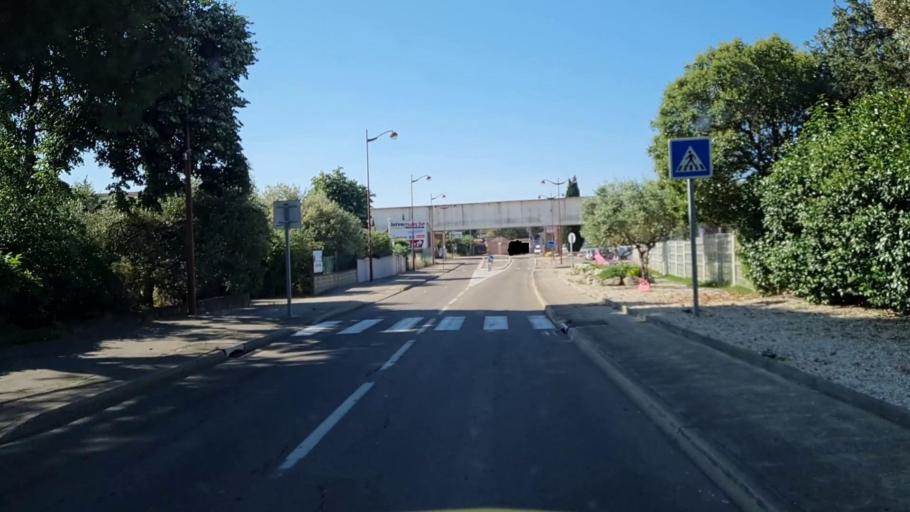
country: FR
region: Languedoc-Roussillon
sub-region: Departement du Gard
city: Saint-Gilles
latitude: 43.6842
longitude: 4.4297
